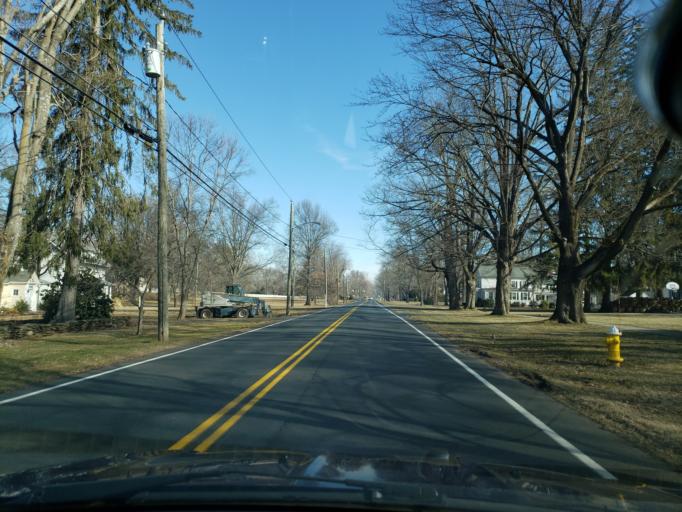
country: US
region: Connecticut
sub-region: Hartford County
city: Suffield Depot
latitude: 41.9710
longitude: -72.6548
